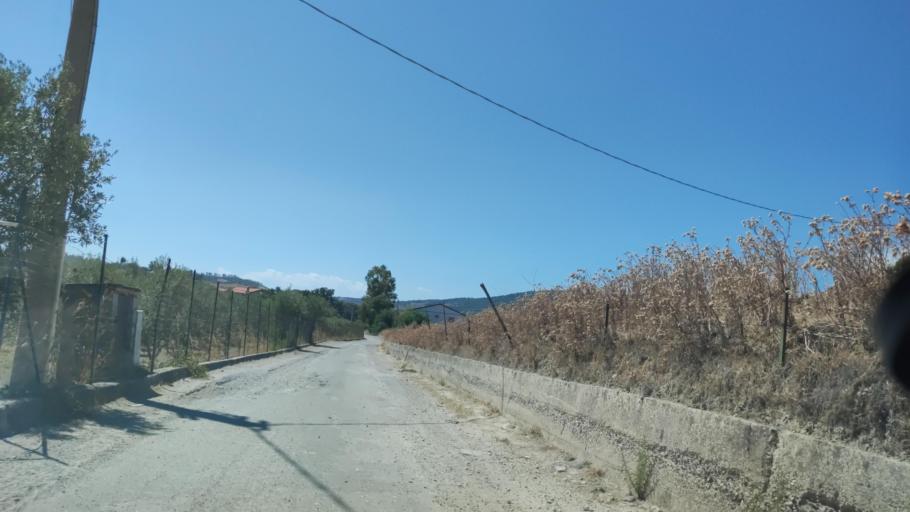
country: IT
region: Calabria
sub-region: Provincia di Reggio Calabria
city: Monasterace
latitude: 38.4401
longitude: 16.5518
